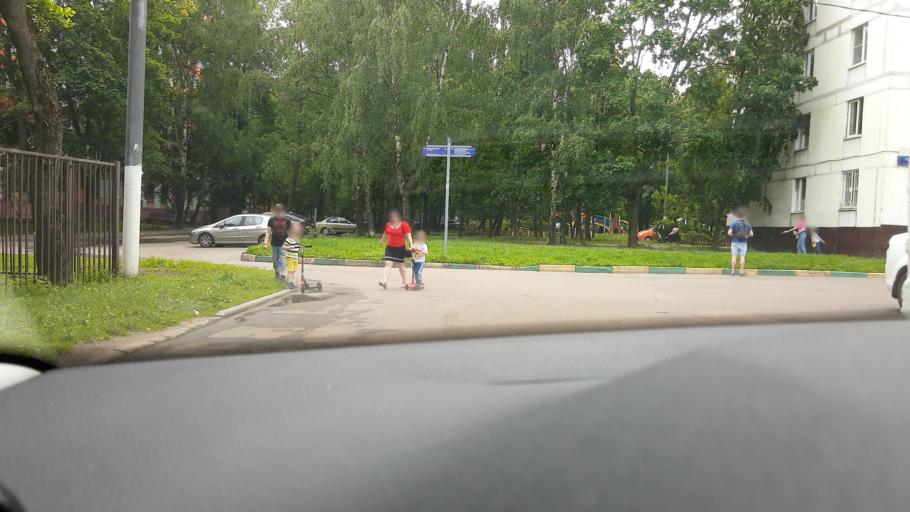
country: RU
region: Moscow
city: Strogino
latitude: 55.8523
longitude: 37.4143
